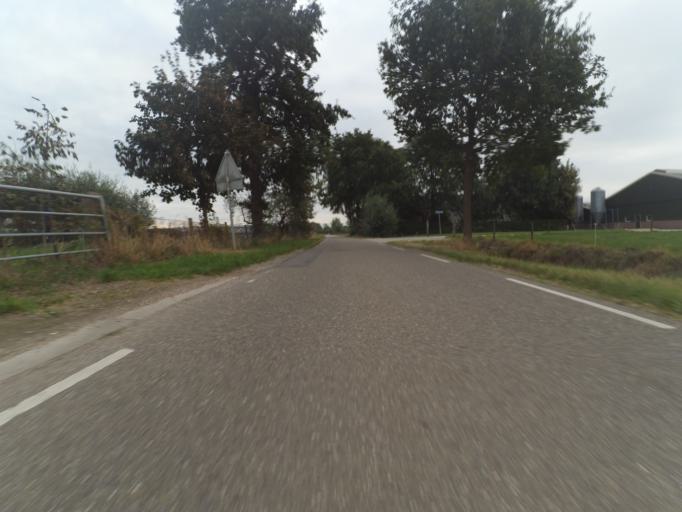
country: NL
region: Utrecht
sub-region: Gemeente Wijk bij Duurstede
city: Wijk bij Duurstede
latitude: 51.9924
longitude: 5.3380
